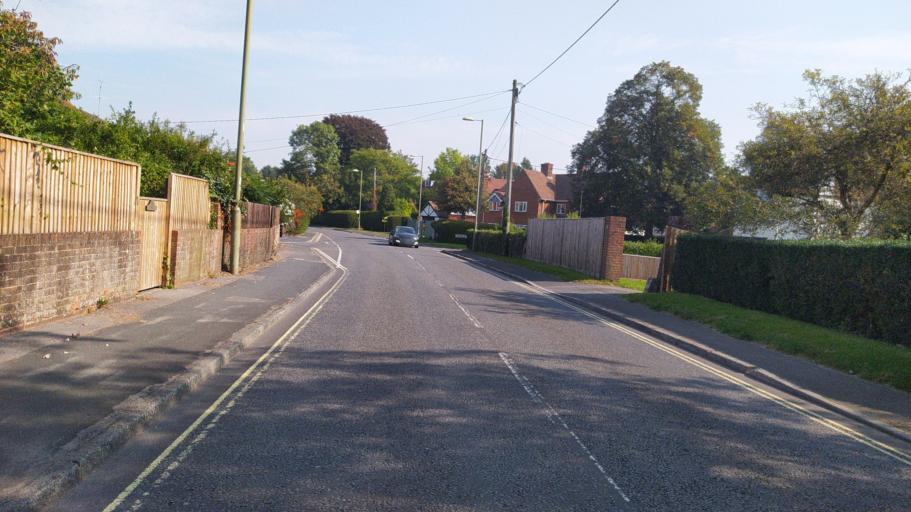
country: GB
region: England
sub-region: Hampshire
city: Andover
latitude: 51.2003
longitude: -1.4798
